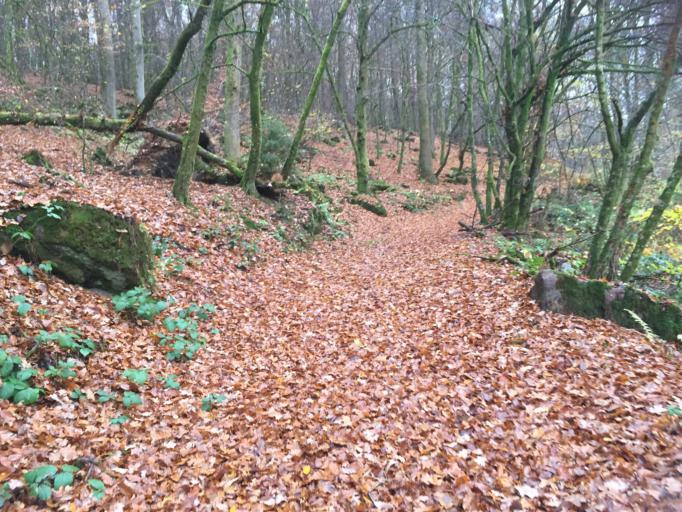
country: DE
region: Hesse
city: Hirschhorn
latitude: 49.4505
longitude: 8.8800
